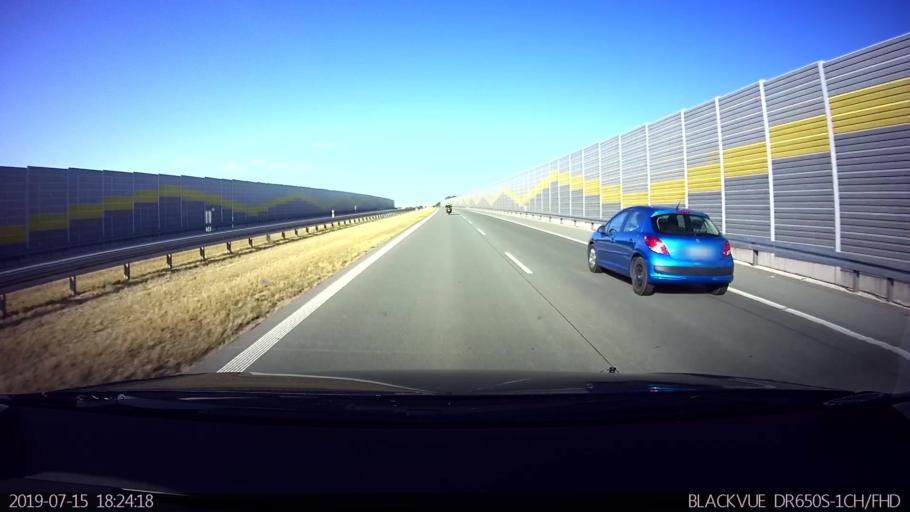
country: PL
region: Lodz Voivodeship
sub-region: Powiat laski
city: Lask
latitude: 51.5655
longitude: 19.1546
